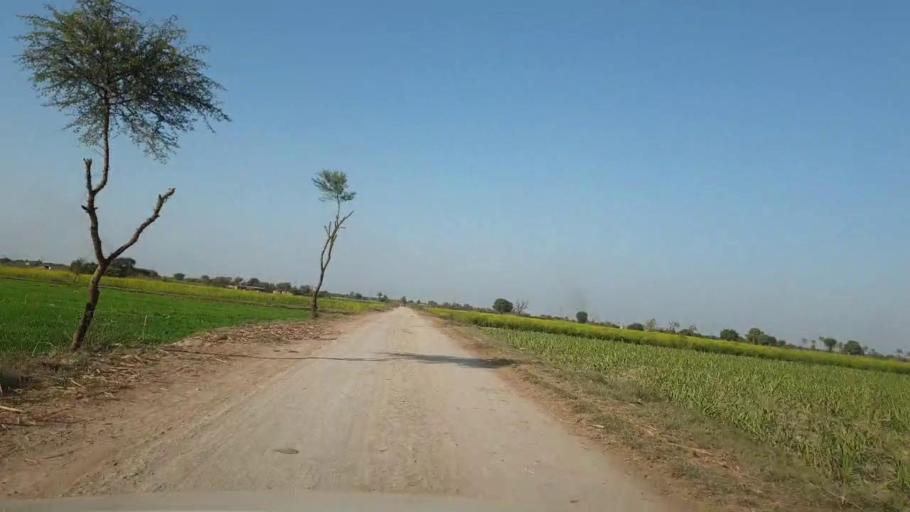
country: PK
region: Sindh
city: Tando Allahyar
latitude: 25.5014
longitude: 68.6541
